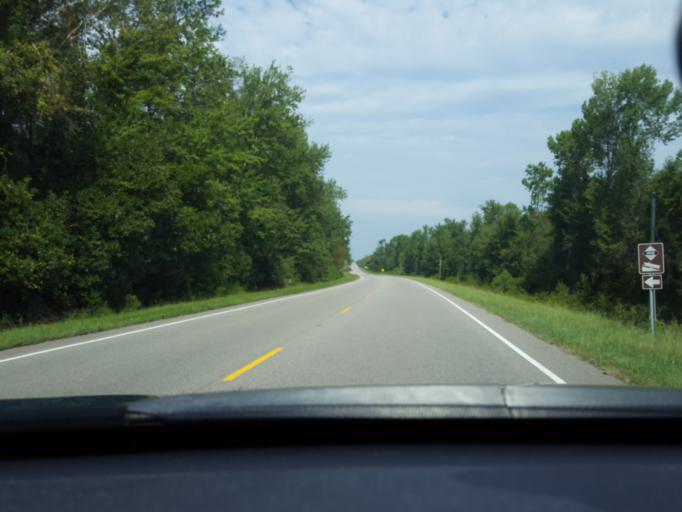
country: US
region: North Carolina
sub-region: Washington County
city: Plymouth
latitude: 35.9094
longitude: -76.7166
